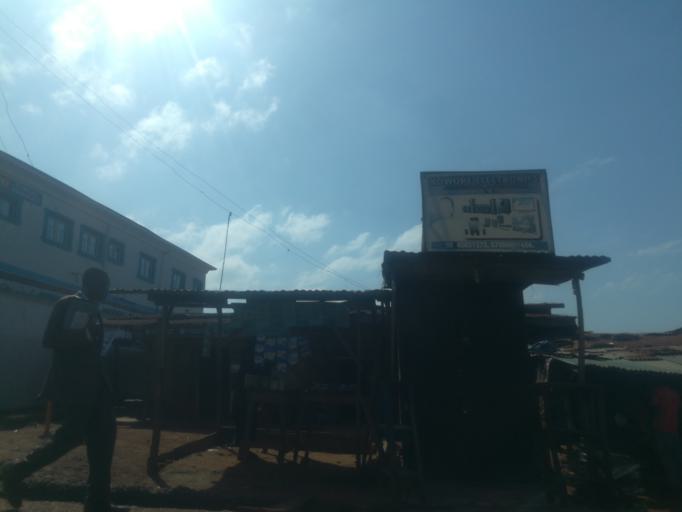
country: NG
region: Oyo
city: Ibadan
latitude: 7.4115
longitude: 3.9526
